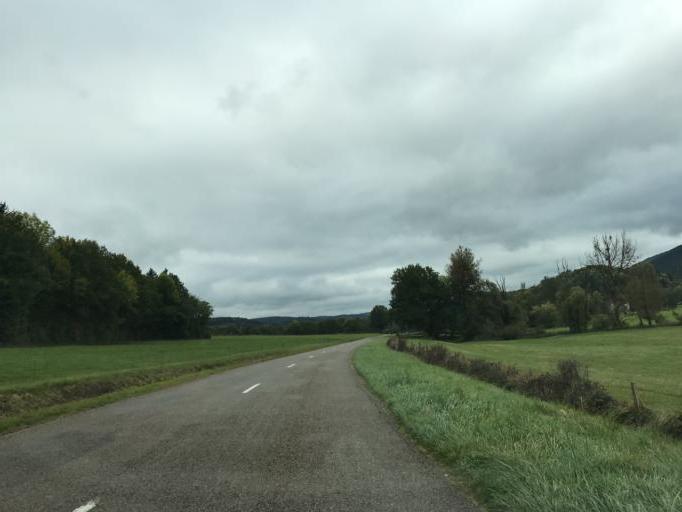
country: FR
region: Rhone-Alpes
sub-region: Departement de l'Ain
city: Cuisiat
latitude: 46.3434
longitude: 5.4387
